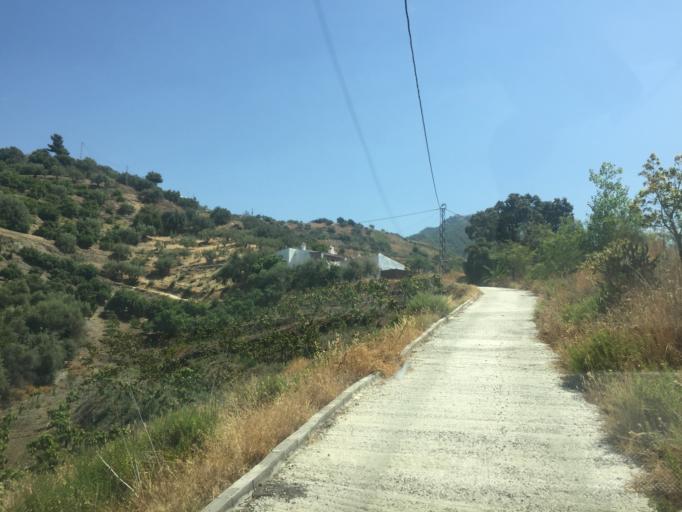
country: ES
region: Andalusia
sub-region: Provincia de Malaga
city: Competa
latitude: 36.8069
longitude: -3.9374
